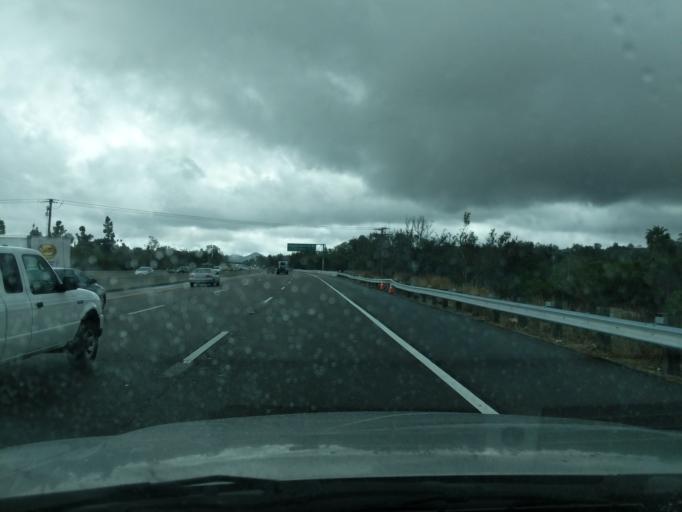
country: US
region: California
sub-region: San Diego County
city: Lake San Marcos
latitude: 33.1586
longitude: -117.2079
